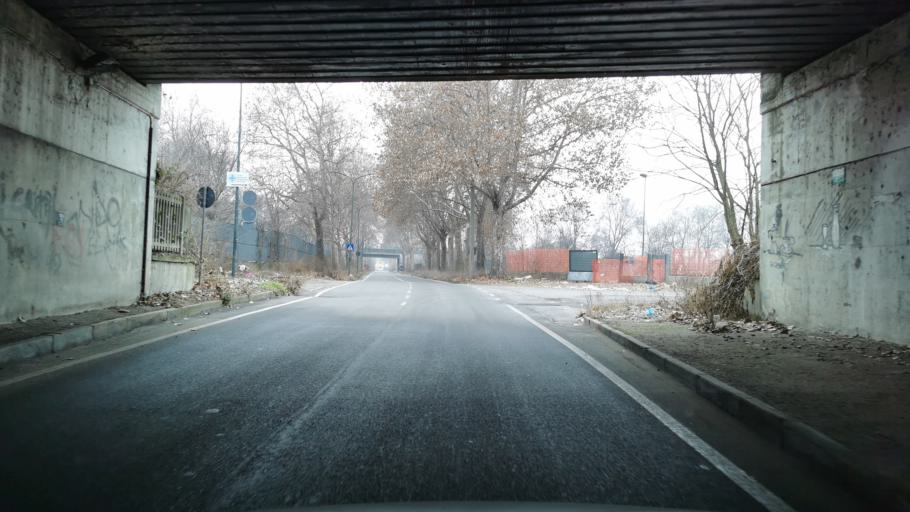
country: IT
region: Piedmont
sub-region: Provincia di Torino
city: Turin
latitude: 45.1157
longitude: 7.6983
